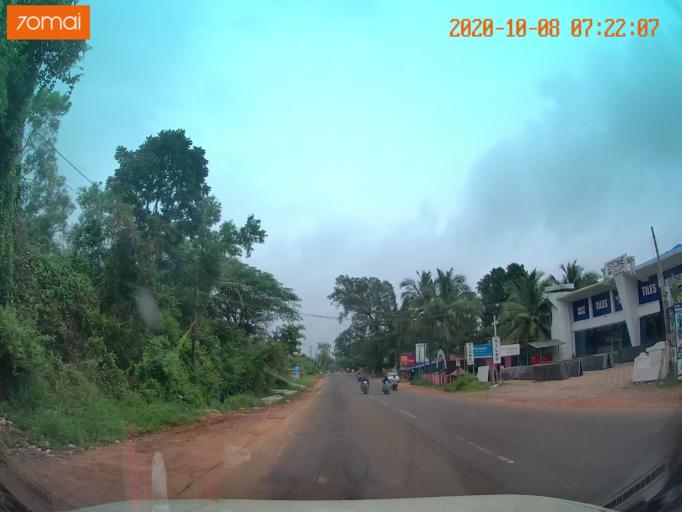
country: IN
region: Kerala
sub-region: Malappuram
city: Tirur
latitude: 10.8611
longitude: 76.0375
